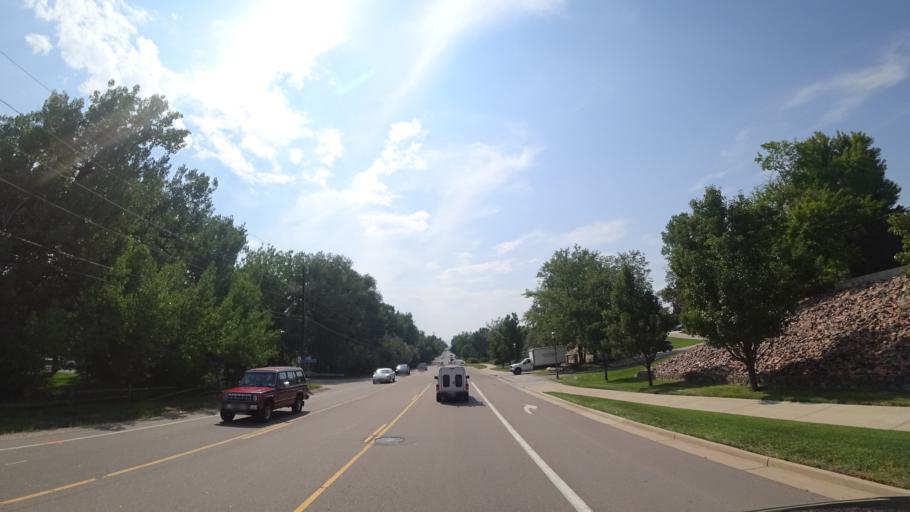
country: US
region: Colorado
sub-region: Arapahoe County
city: Greenwood Village
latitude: 39.6097
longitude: -104.9721
